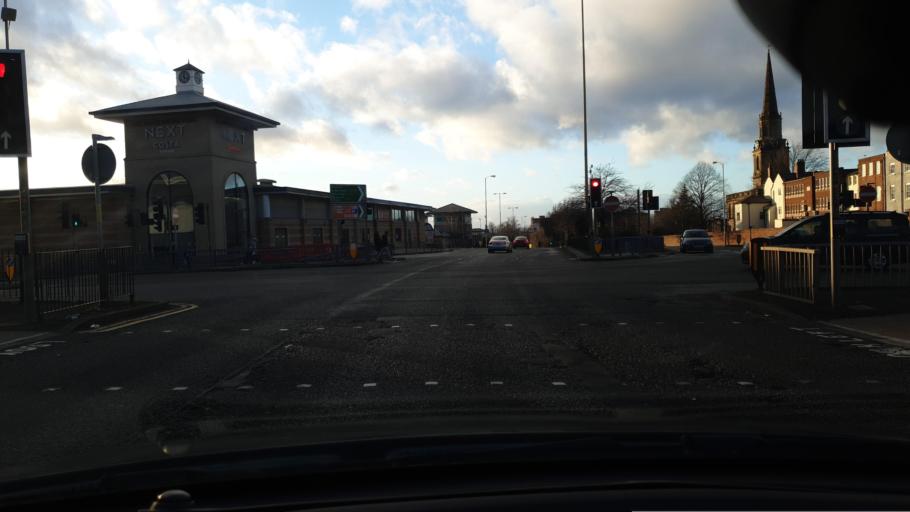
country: GB
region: England
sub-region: Wolverhampton
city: Wolverhampton
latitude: 52.5806
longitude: -2.1252
